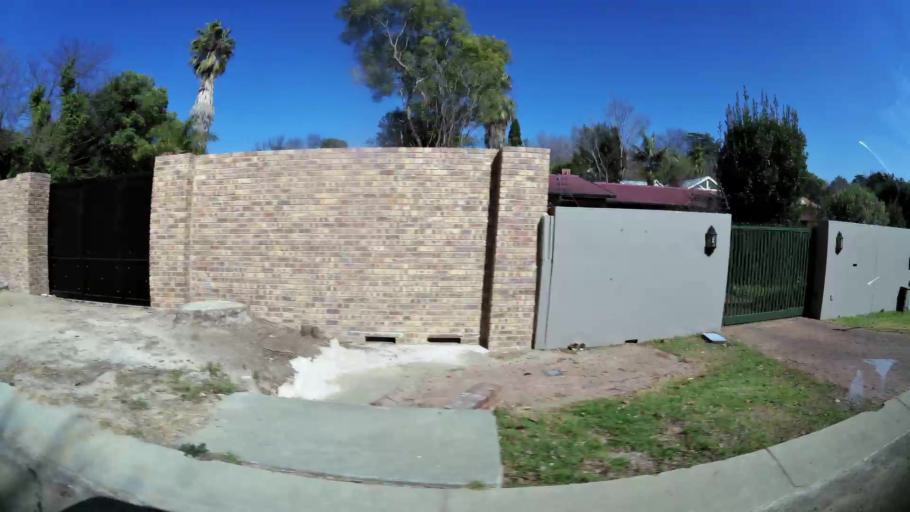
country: ZA
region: Gauteng
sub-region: City of Johannesburg Metropolitan Municipality
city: Johannesburg
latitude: -26.1024
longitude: 28.0388
